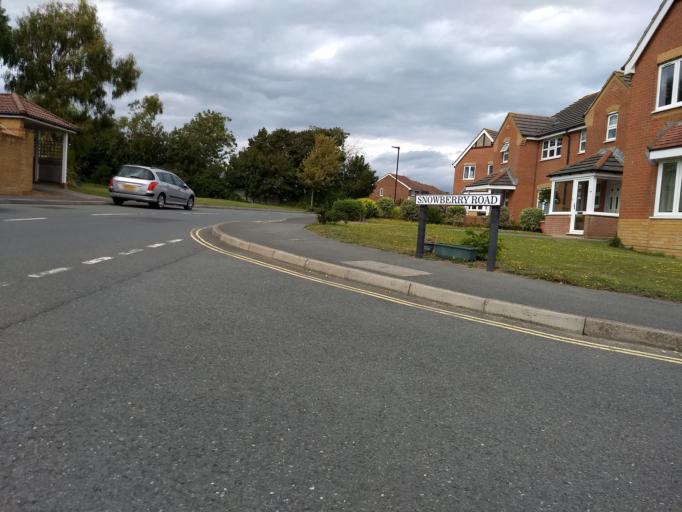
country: GB
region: England
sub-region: Isle of Wight
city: Newport
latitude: 50.7004
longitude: -1.3061
